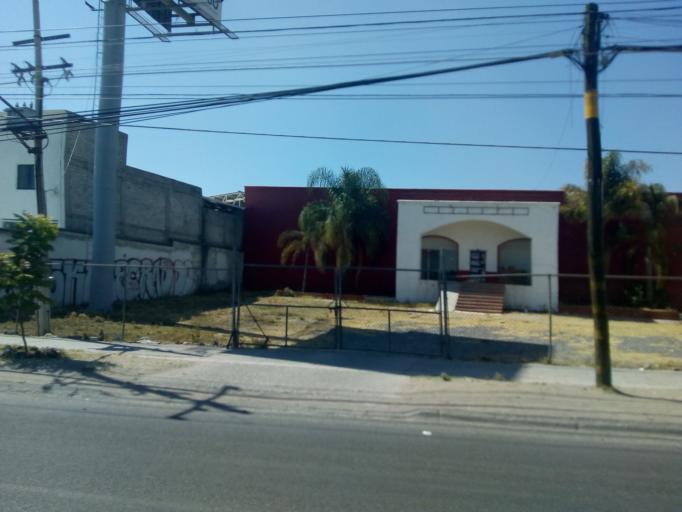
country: MX
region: Guanajuato
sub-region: Leon
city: Centro Familiar la Soledad
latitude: 21.0946
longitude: -101.7309
